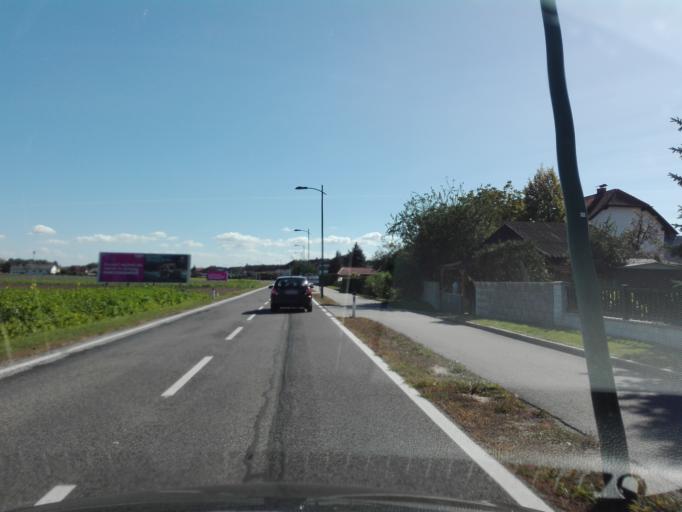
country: AT
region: Lower Austria
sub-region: Politischer Bezirk Amstetten
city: Ennsdorf
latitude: 48.2083
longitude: 14.4973
